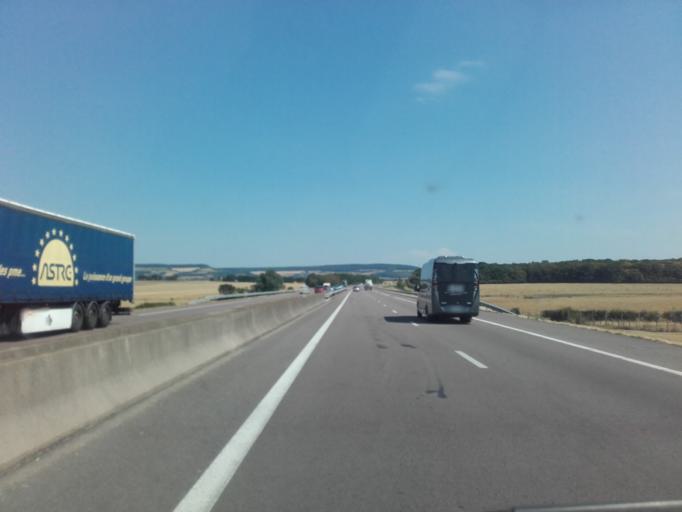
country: FR
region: Bourgogne
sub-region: Departement de la Cote-d'Or
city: Vitteaux
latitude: 47.3550
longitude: 4.4389
